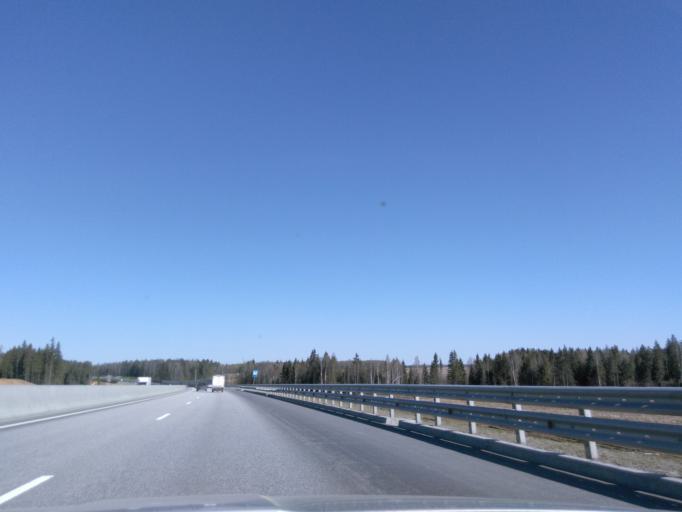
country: RU
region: Moskovskaya
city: Mendeleyevo
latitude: 56.0857
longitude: 37.2055
